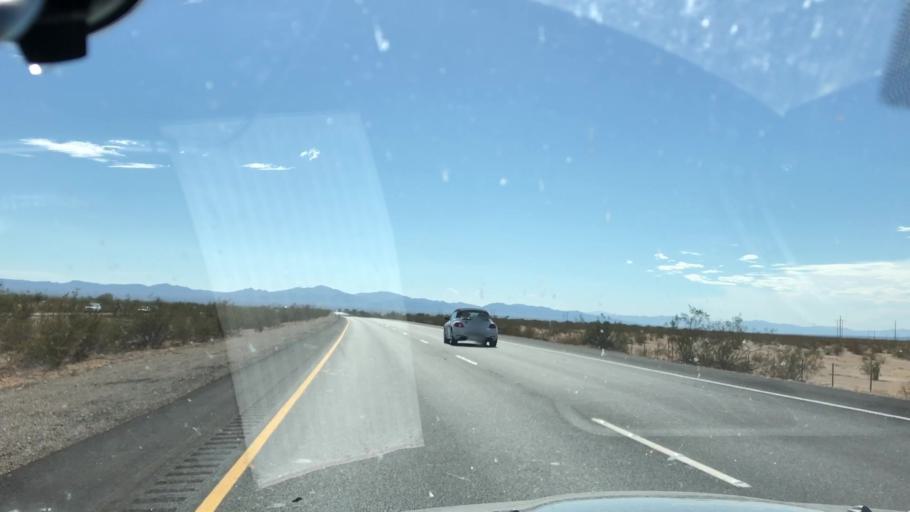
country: US
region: California
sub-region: Riverside County
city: Mesa Verde
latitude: 33.6078
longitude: -114.9072
